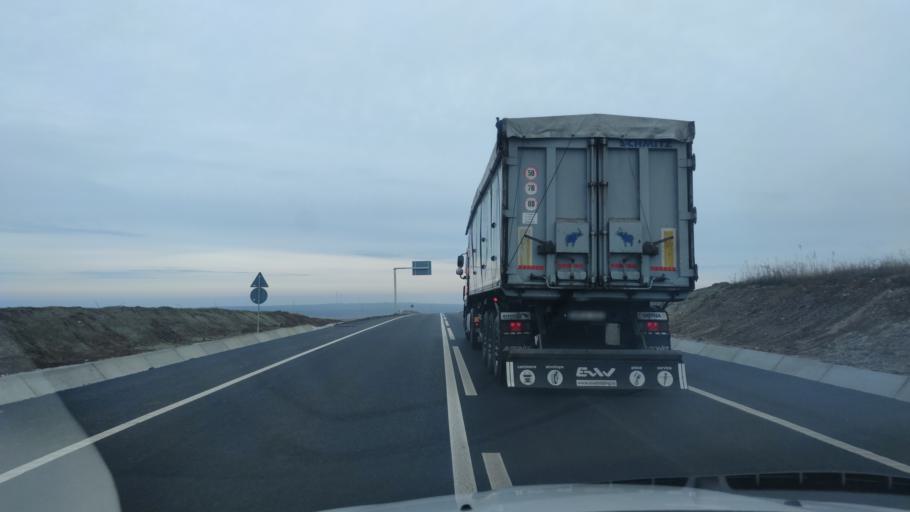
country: RO
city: Szekelyhid
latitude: 47.3544
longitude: 22.1283
